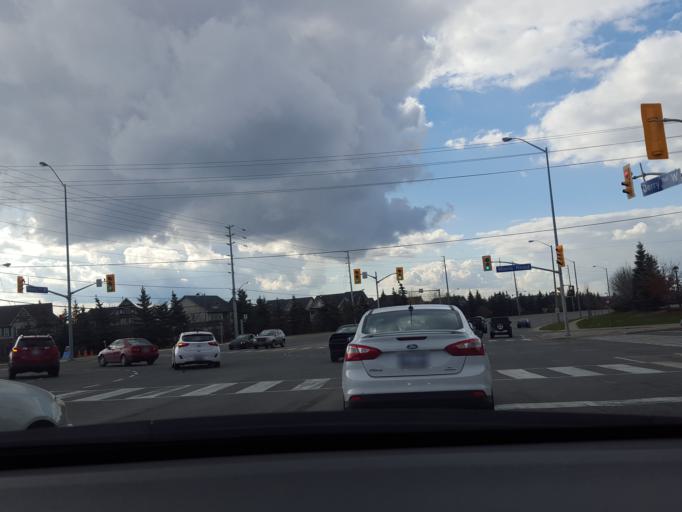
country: CA
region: Ontario
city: Brampton
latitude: 43.6330
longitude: -79.7221
